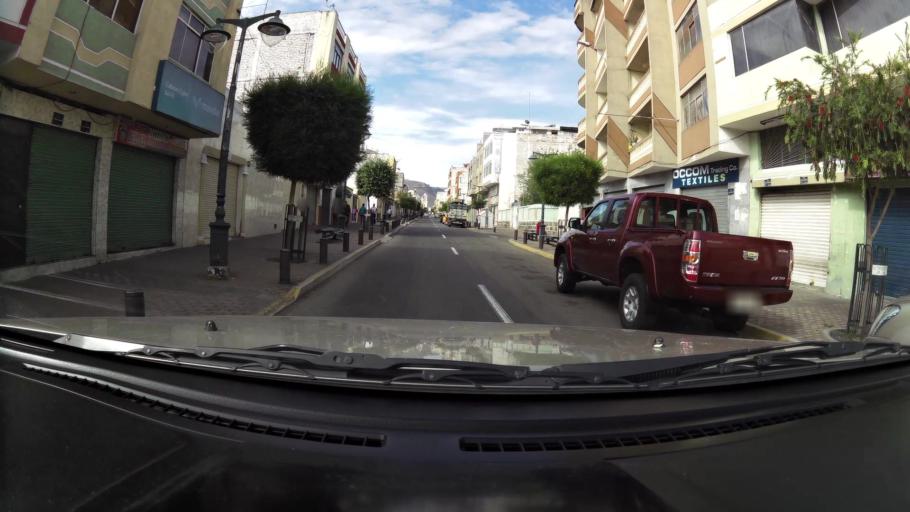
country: EC
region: Tungurahua
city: Ambato
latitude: -1.2504
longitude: -78.6395
